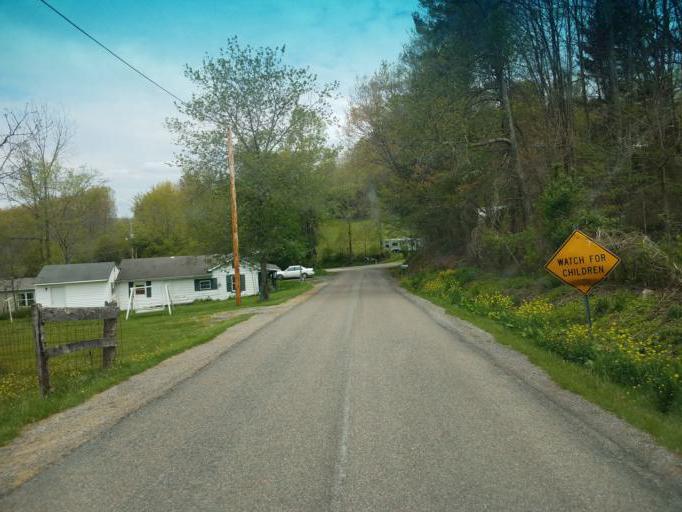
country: US
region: Virginia
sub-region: Smyth County
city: Marion
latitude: 36.8041
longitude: -81.4638
